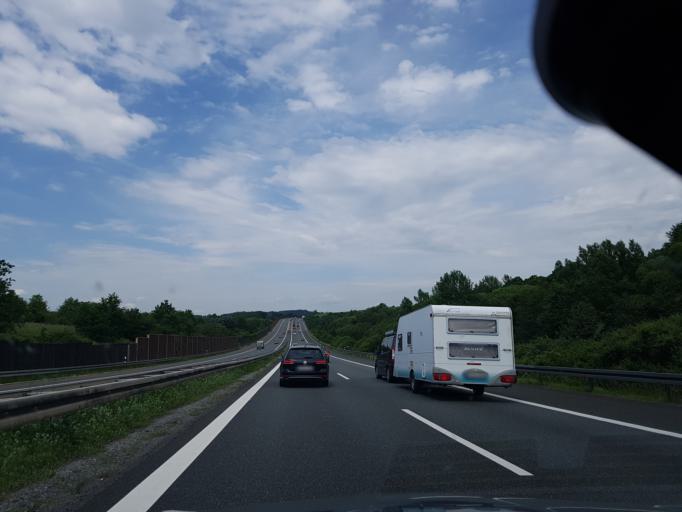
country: DE
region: Saxony
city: Neuensalz
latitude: 50.4828
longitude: 12.1863
